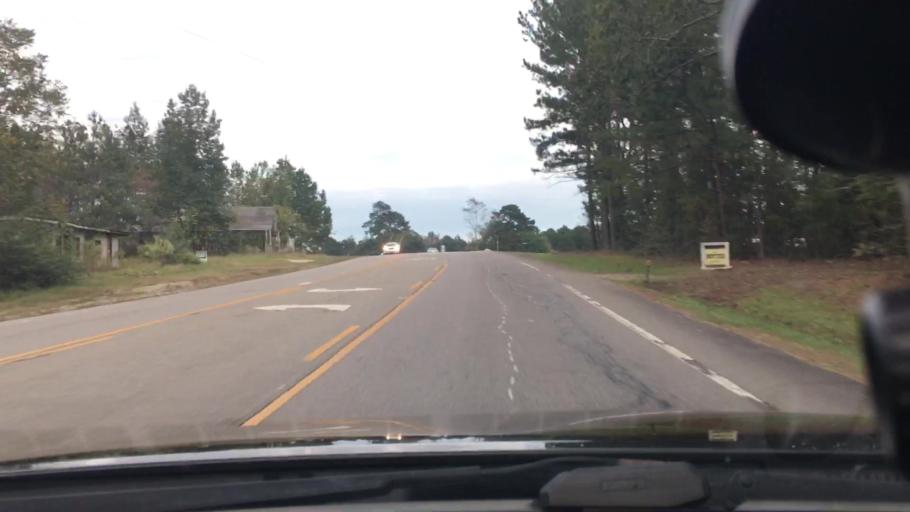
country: US
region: North Carolina
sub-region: Moore County
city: Carthage
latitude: 35.3489
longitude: -79.3612
